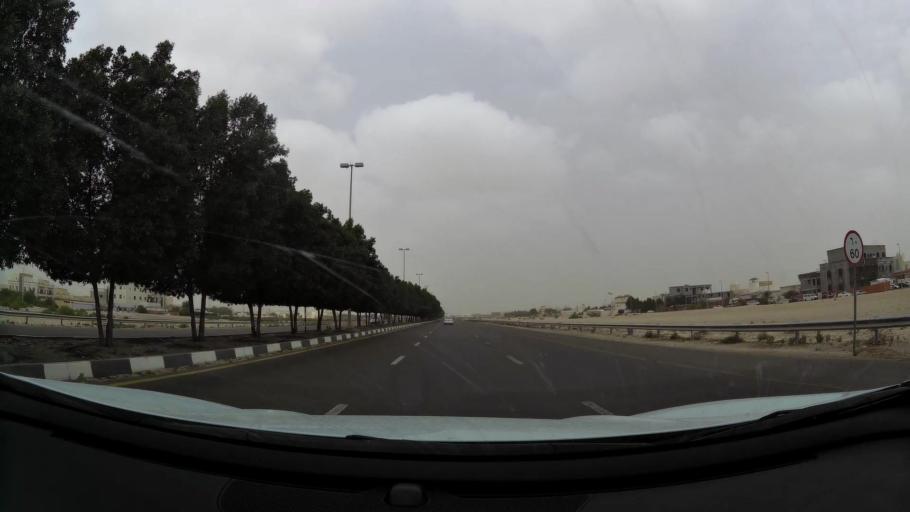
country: AE
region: Abu Dhabi
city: Abu Dhabi
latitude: 24.3928
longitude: 54.7184
